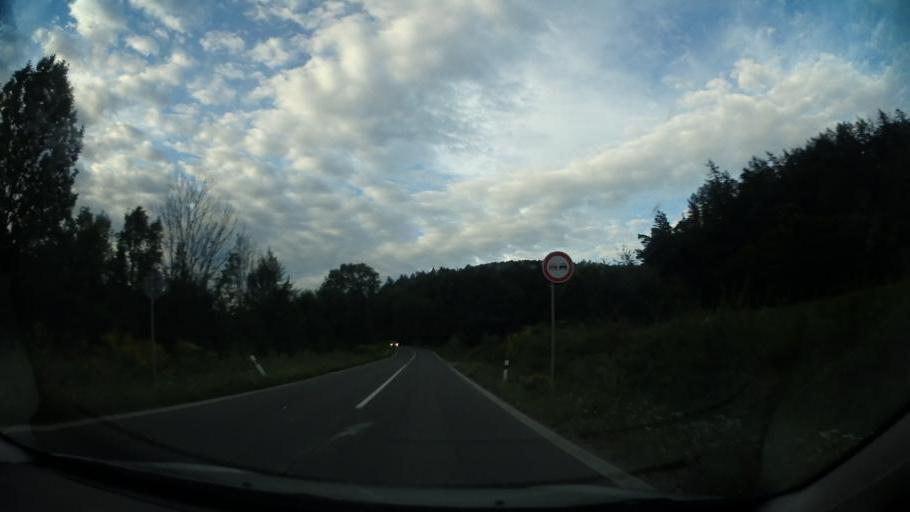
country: CZ
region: Olomoucky
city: Paseka
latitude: 49.8237
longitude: 17.2063
